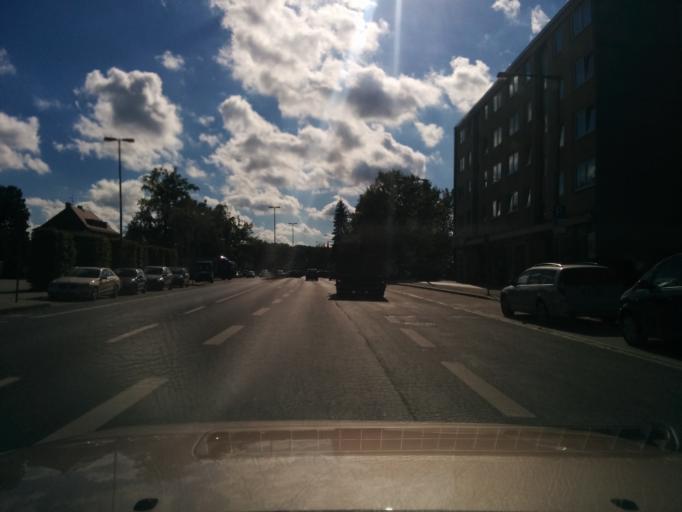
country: DE
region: Bavaria
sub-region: Regierungsbezirk Mittelfranken
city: Nuernberg
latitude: 49.4853
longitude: 11.1051
